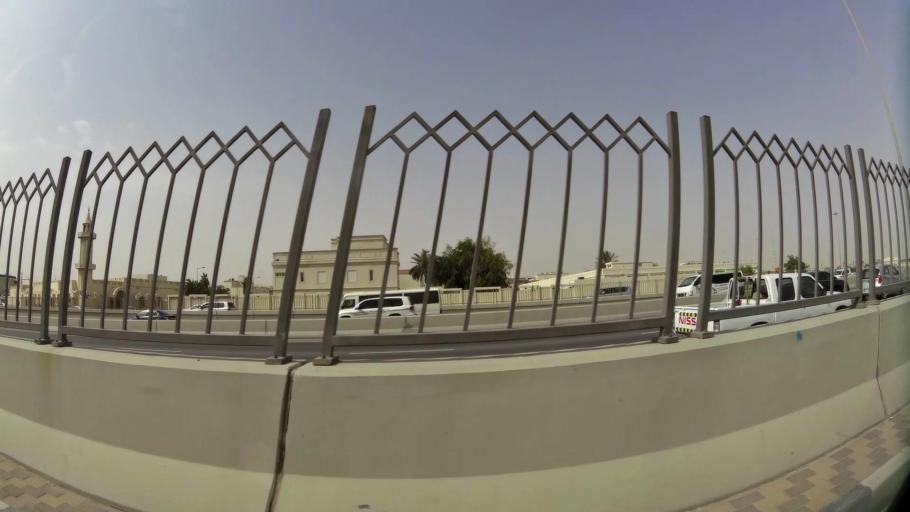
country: QA
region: Baladiyat ad Dawhah
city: Doha
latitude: 25.2791
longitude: 51.4868
